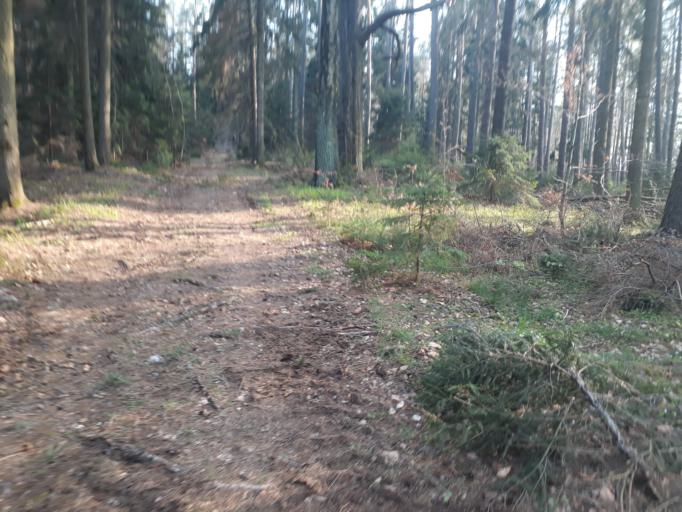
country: DE
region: Saxony
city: Reinhardtsgrimma
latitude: 50.8948
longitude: 13.7819
